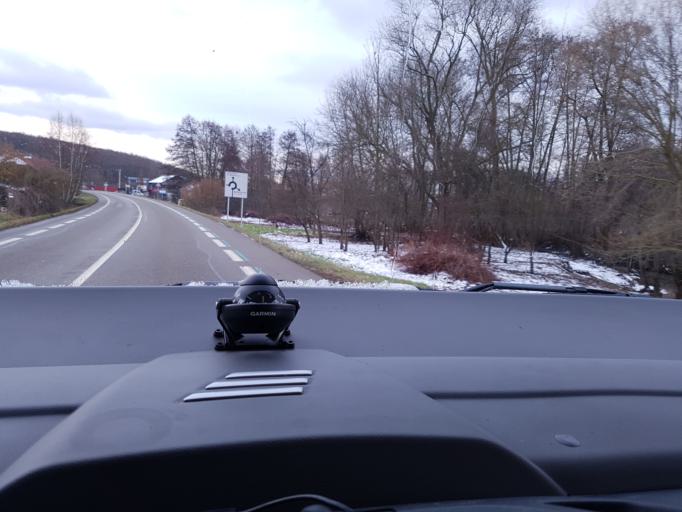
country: FR
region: Alsace
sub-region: Departement du Bas-Rhin
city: Ville
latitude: 48.3378
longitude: 7.3216
